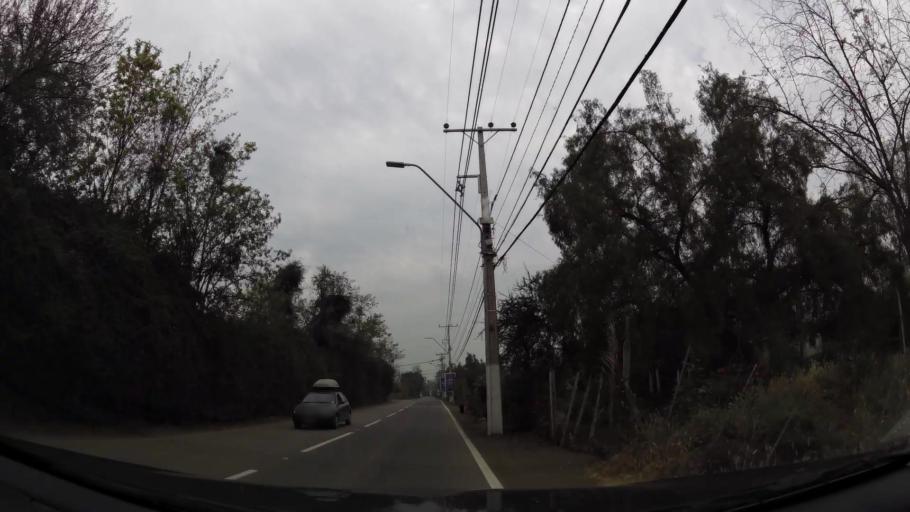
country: CL
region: Santiago Metropolitan
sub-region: Provincia de Chacabuco
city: Chicureo Abajo
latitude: -33.2099
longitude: -70.6616
